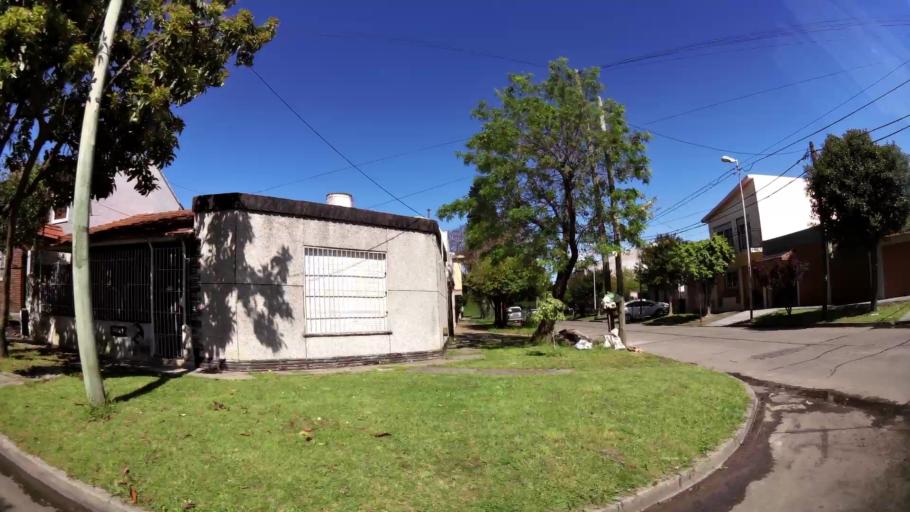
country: AR
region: Buenos Aires
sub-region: Partido de Quilmes
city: Quilmes
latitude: -34.6975
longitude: -58.3030
